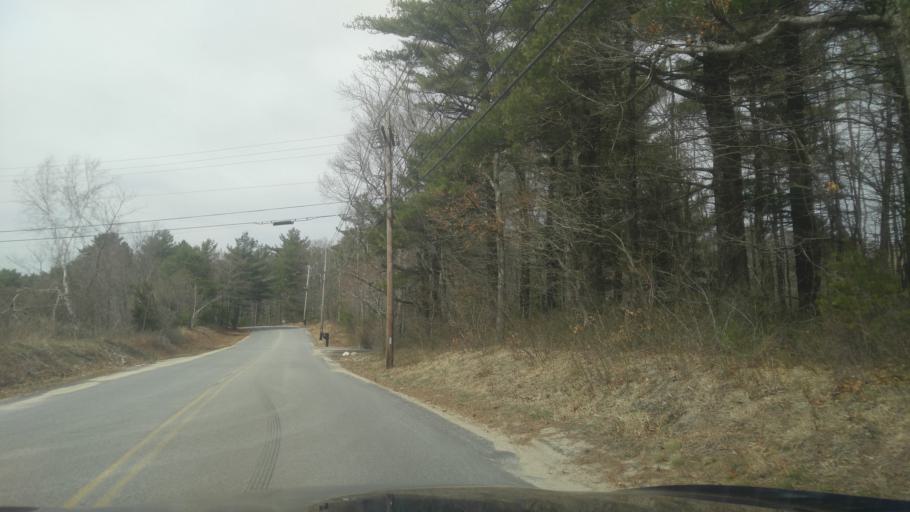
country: US
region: Rhode Island
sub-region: Washington County
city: Exeter
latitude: 41.6219
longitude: -71.5642
